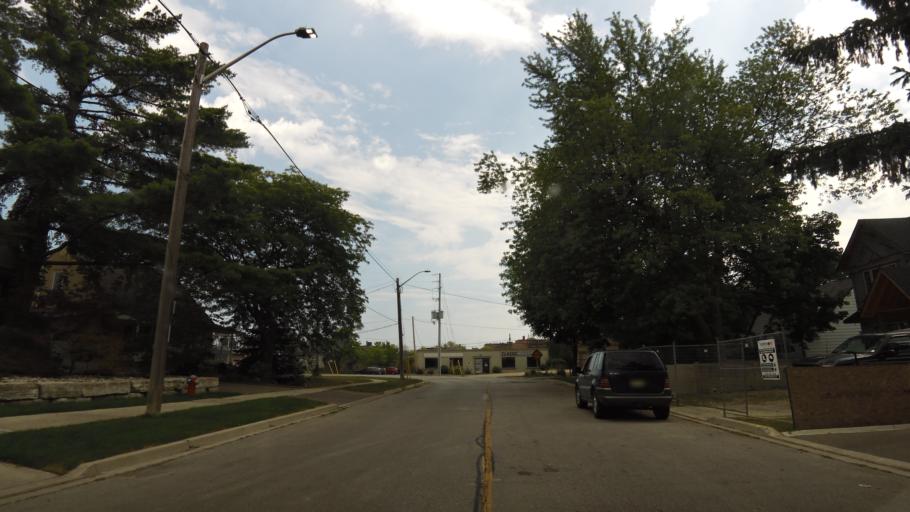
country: CA
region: Ontario
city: Mississauga
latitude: 43.5661
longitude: -79.5783
